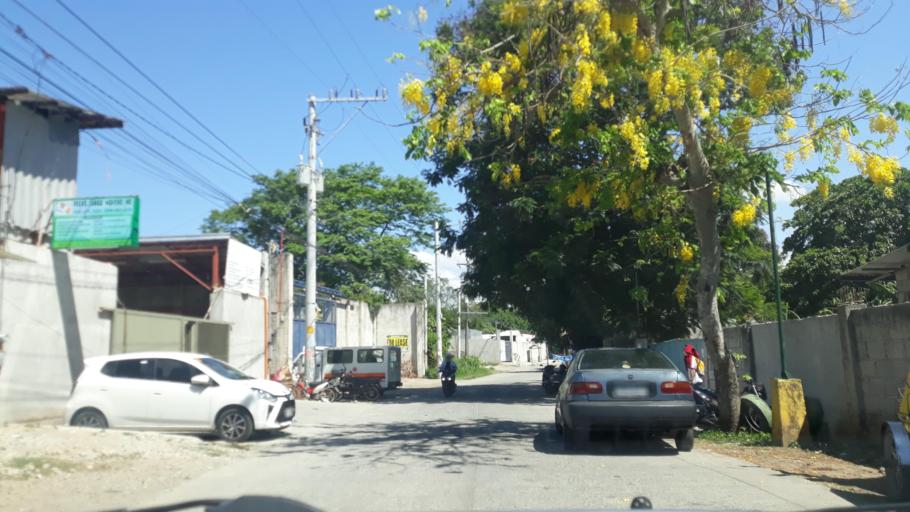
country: PH
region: Calabarzon
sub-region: Province of Cavite
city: Manggahan
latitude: 14.2989
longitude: 120.9170
